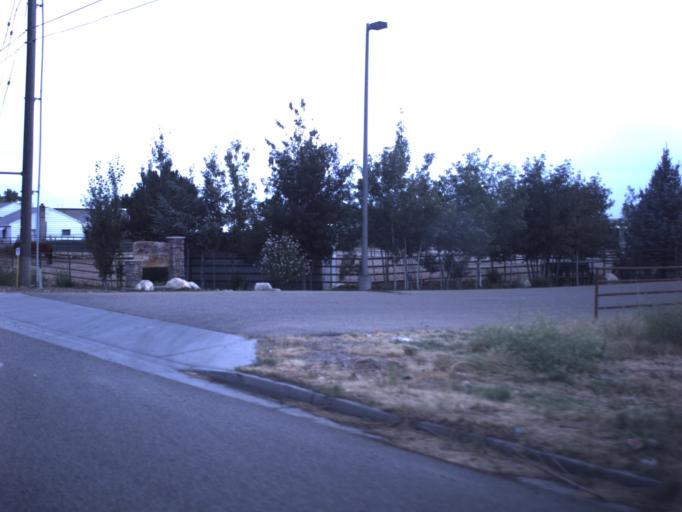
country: US
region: Utah
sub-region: Weber County
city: West Haven
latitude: 41.2168
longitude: -112.0258
